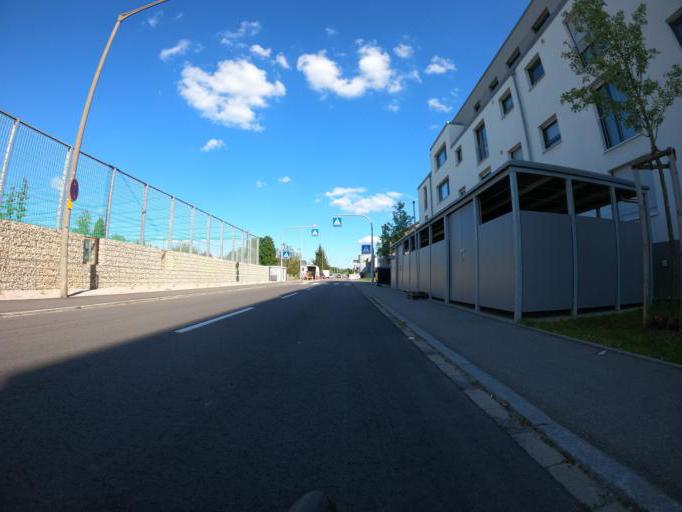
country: DE
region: Baden-Wuerttemberg
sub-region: Regierungsbezirk Stuttgart
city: Magstadt
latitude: 48.7378
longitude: 8.9675
